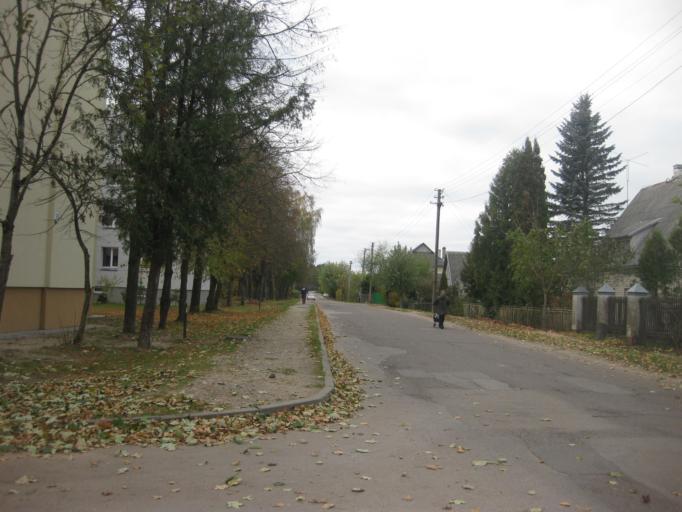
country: LT
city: Ezerelis
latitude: 54.8830
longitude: 23.6067
